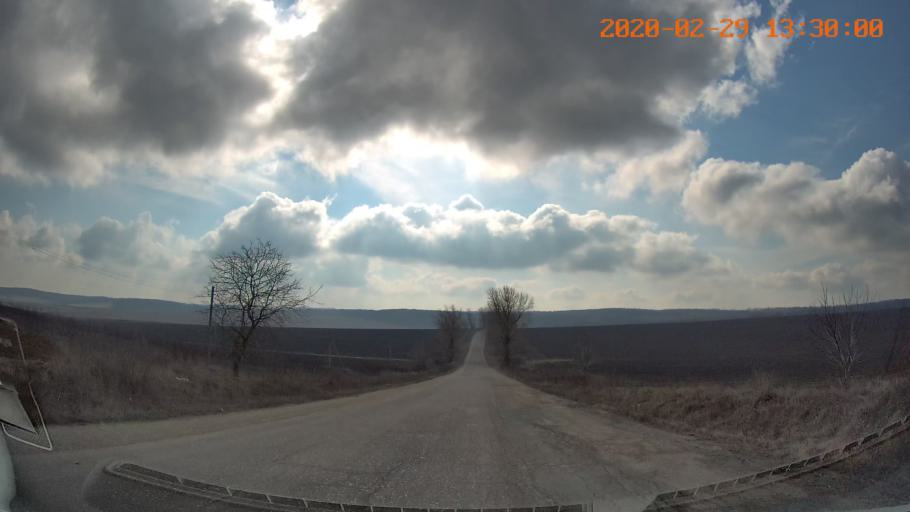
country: MD
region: Telenesti
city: Camenca
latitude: 47.8912
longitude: 28.6323
